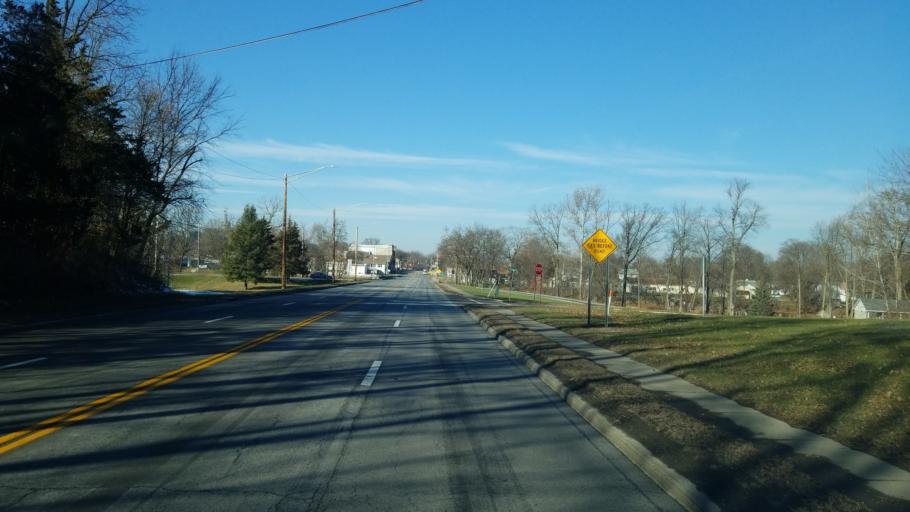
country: US
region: Ohio
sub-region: Huron County
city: Monroeville
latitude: 41.2399
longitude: -82.6925
